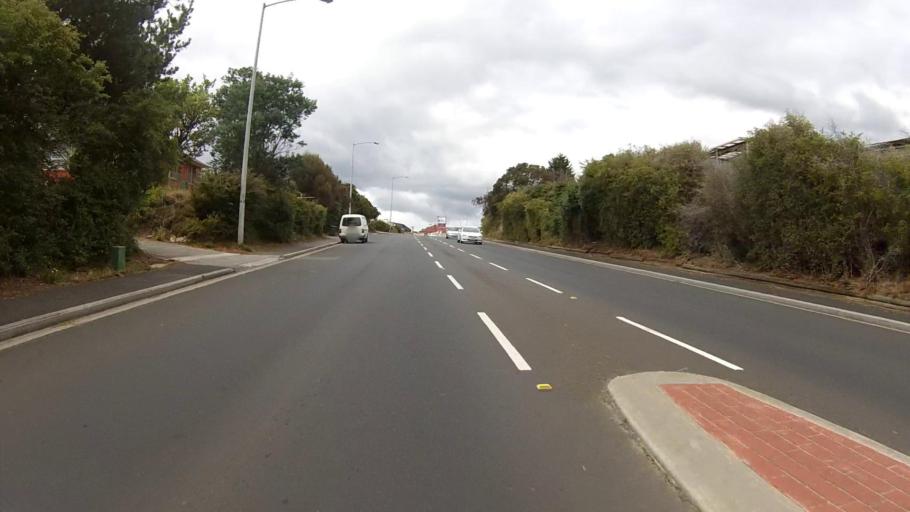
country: AU
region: Tasmania
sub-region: Glenorchy
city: Claremont
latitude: -42.7878
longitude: 147.2523
